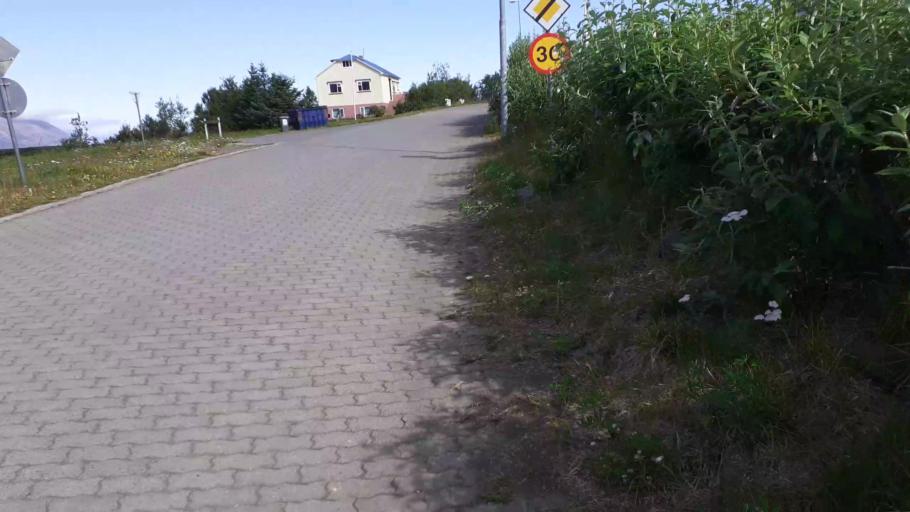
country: IS
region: Northeast
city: Dalvik
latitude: 65.9818
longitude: -18.3802
